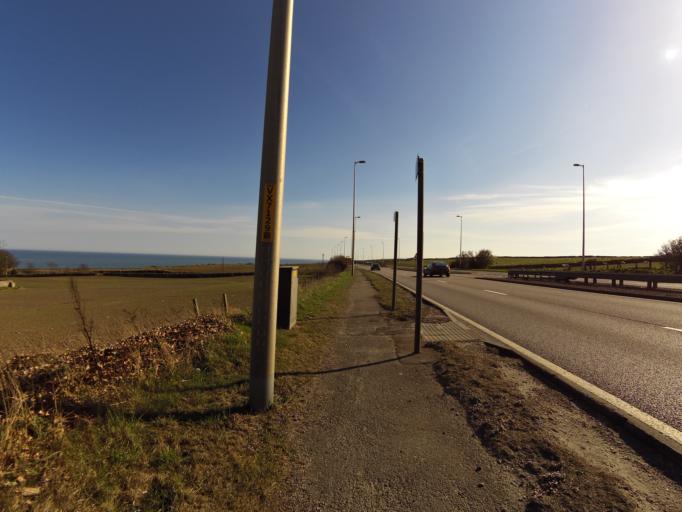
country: GB
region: Scotland
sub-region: Aberdeenshire
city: Newtonhill
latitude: 57.0187
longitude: -2.1680
